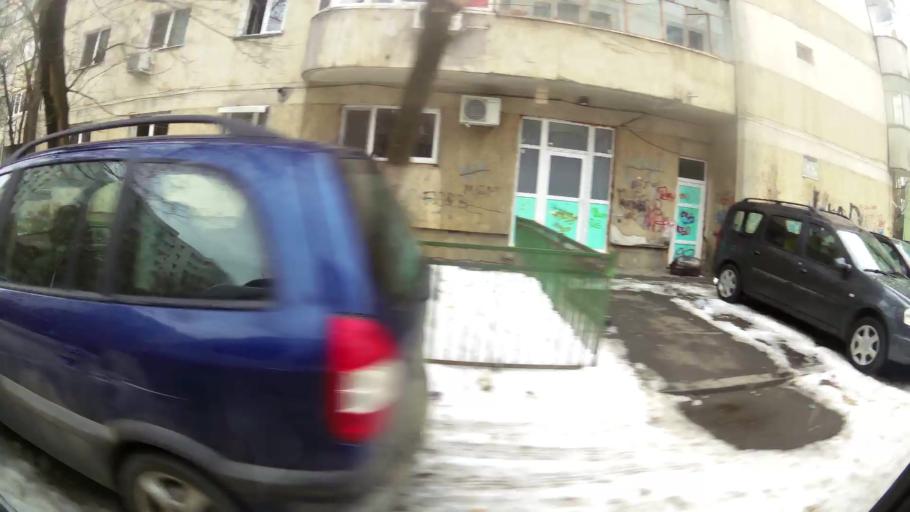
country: RO
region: Bucuresti
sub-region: Municipiul Bucuresti
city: Bucuresti
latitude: 44.4089
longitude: 26.0612
